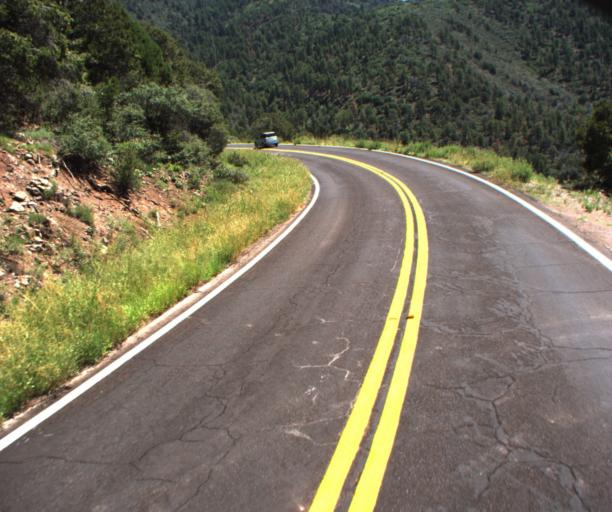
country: US
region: Arizona
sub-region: Greenlee County
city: Morenci
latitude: 33.4279
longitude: -109.3757
